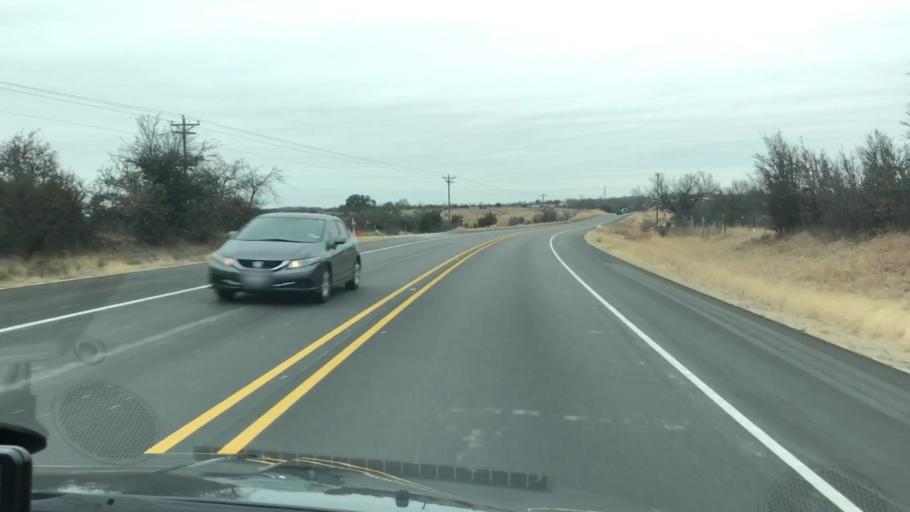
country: US
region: Texas
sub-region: Erath County
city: Stephenville
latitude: 32.4630
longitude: -98.1427
